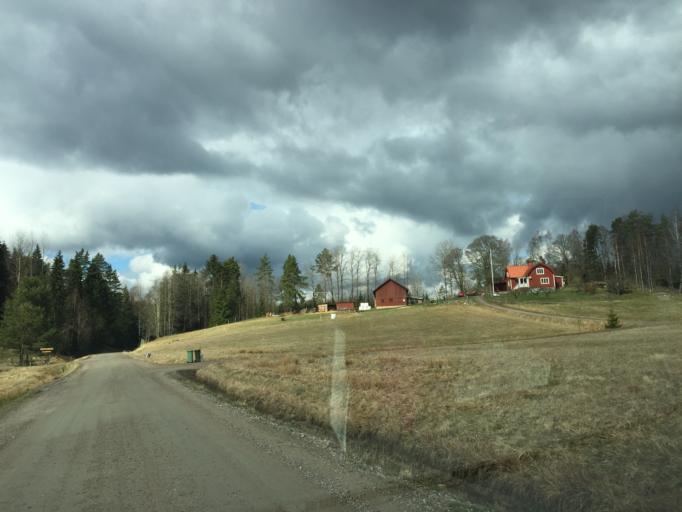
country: SE
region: Soedermanland
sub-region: Nykopings Kommun
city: Nykoping
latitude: 58.9603
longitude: 17.0484
